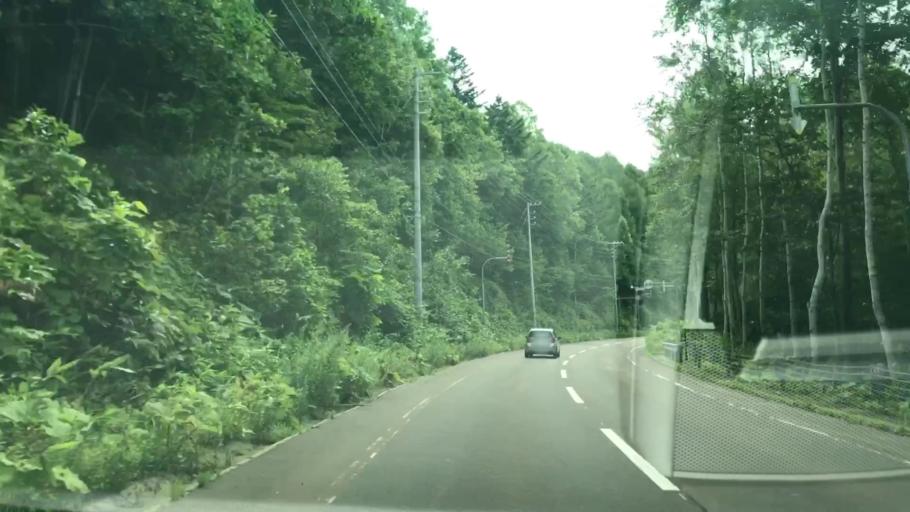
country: JP
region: Hokkaido
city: Yoichi
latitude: 43.1277
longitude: 140.8283
